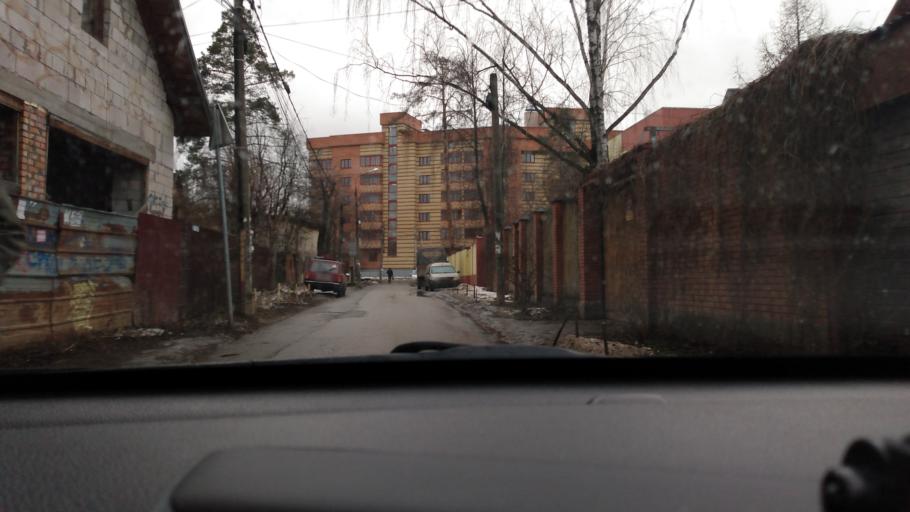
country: RU
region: Moskovskaya
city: Druzhba
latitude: 55.8971
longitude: 37.7435
